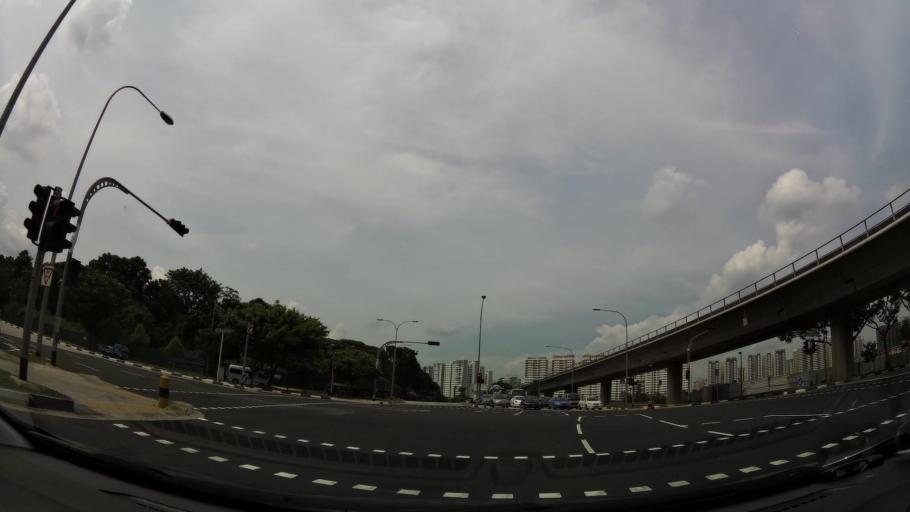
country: MY
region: Johor
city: Johor Bahru
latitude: 1.3689
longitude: 103.7486
